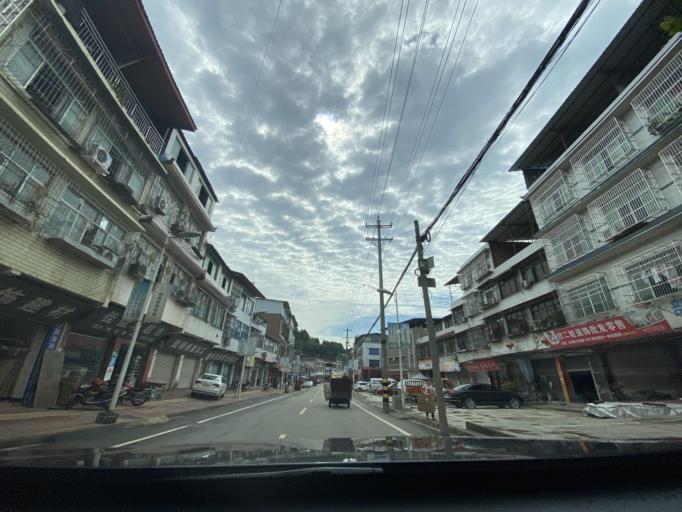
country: CN
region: Sichuan
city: Jiancheng
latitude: 30.4874
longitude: 104.6307
